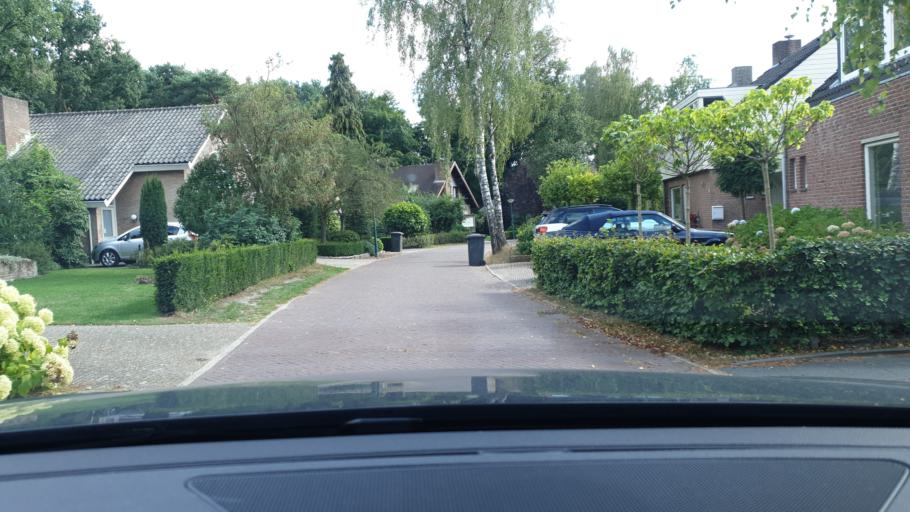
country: NL
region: North Brabant
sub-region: Gemeente Waalre
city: Waalre
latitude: 51.3919
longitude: 5.4484
